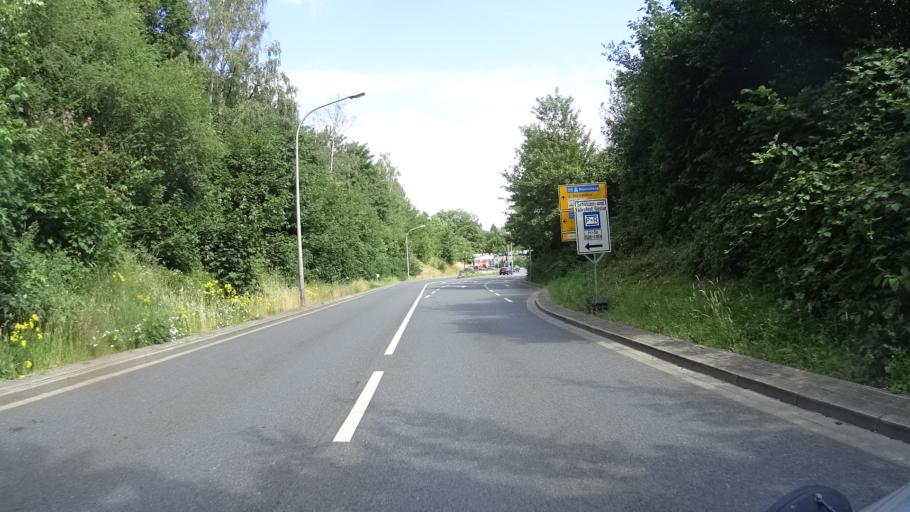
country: DE
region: Lower Saxony
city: Goslar
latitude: 51.9108
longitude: 10.4169
